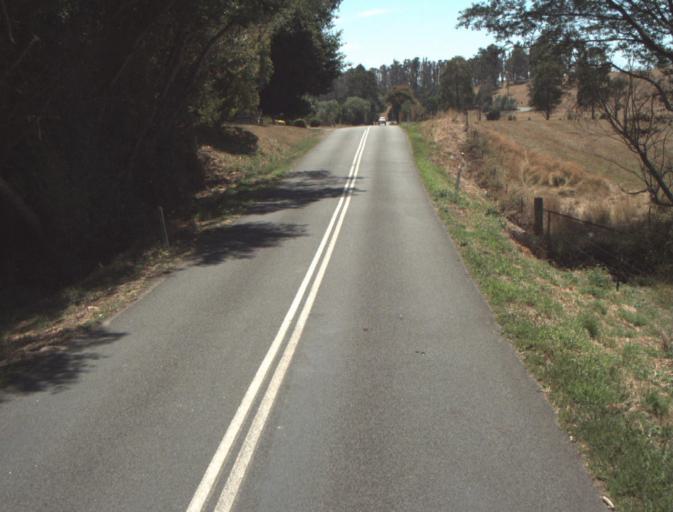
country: AU
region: Tasmania
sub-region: Launceston
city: Mayfield
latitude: -41.2643
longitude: 147.1349
